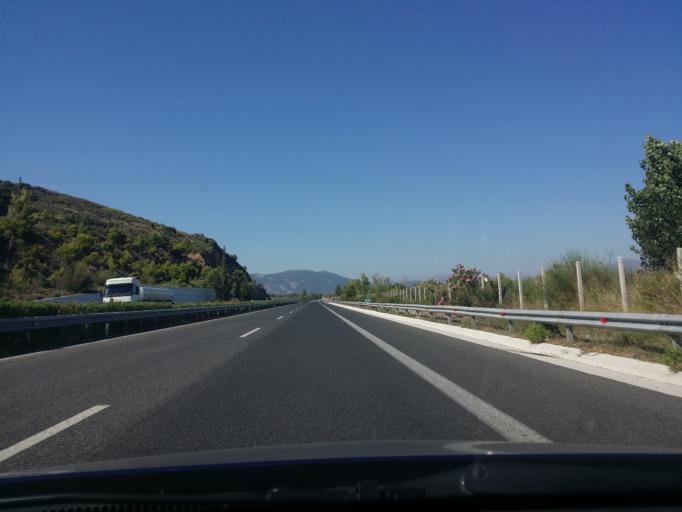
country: GR
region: Peloponnese
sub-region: Nomos Korinthias
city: Khiliomodhi
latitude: 37.8570
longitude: 22.8339
